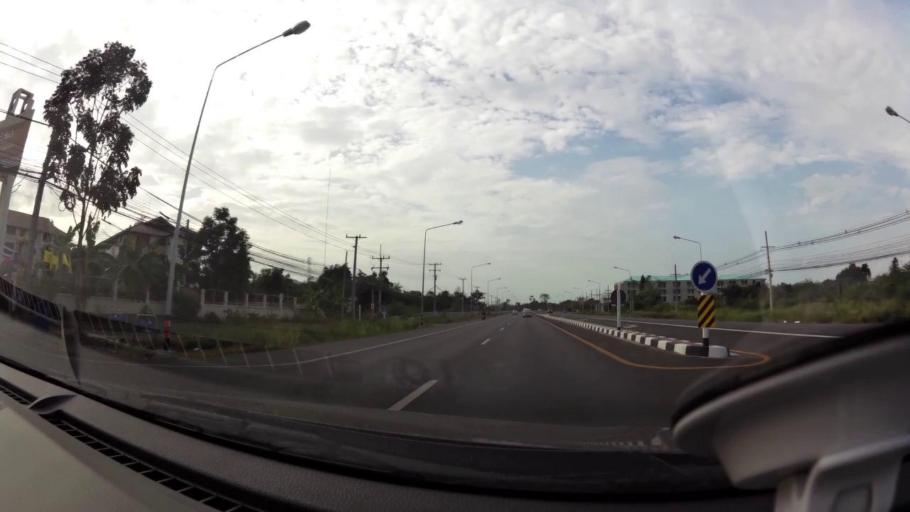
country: TH
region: Prachuap Khiri Khan
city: Hua Hin
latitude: 12.4766
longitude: 99.9712
